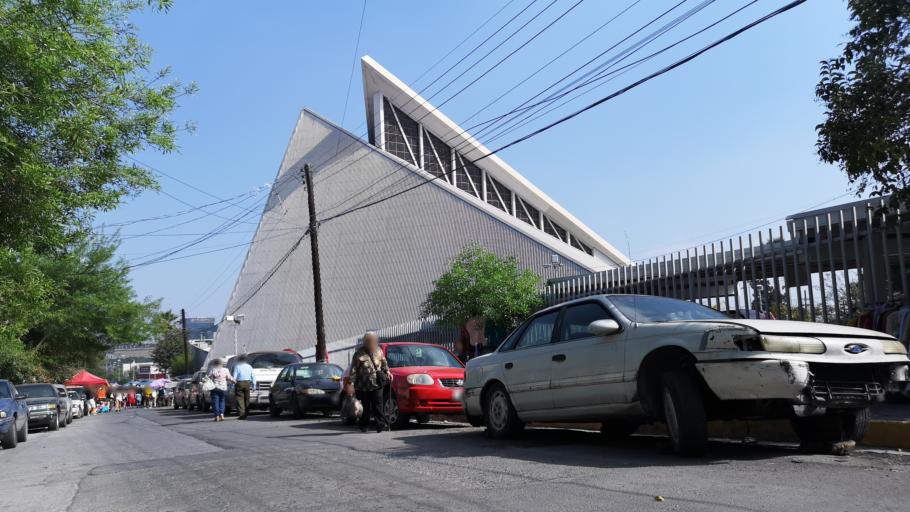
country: MX
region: Nuevo Leon
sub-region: Monterrey
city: Monterrey
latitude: 25.6571
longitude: -100.3151
